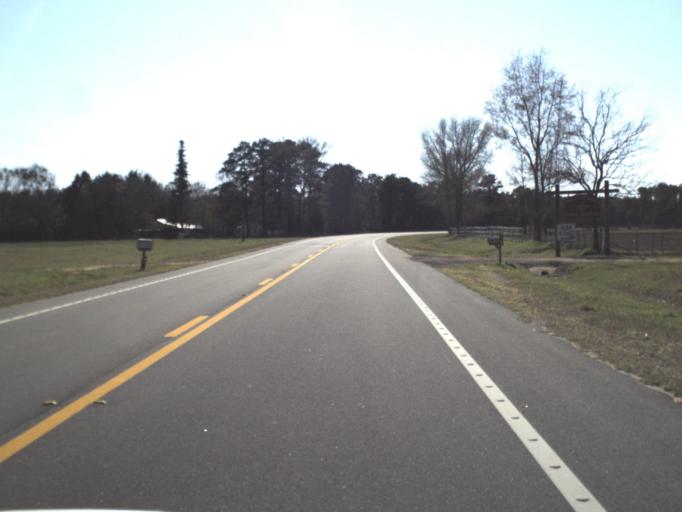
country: US
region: Florida
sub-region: Calhoun County
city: Blountstown
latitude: 30.4353
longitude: -85.2258
